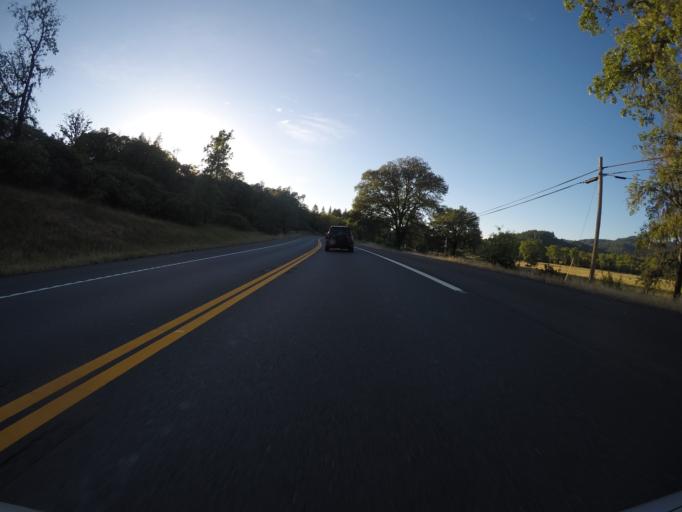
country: US
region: California
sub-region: Mendocino County
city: Laytonville
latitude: 39.6406
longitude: -123.4716
